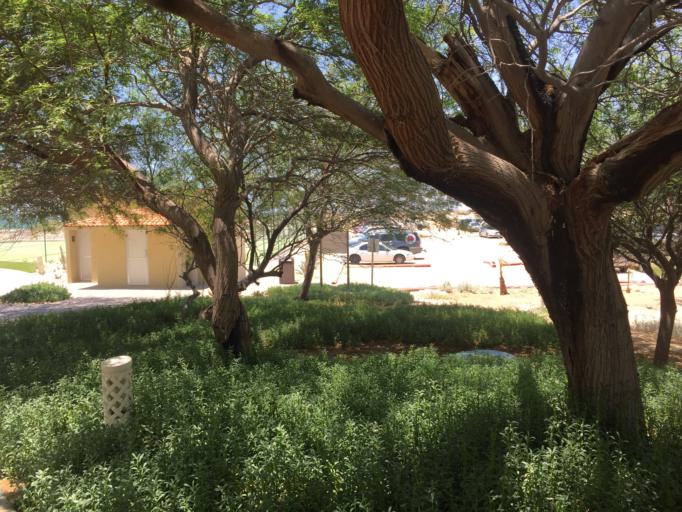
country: MX
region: Sonora
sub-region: Puerto Penasco
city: Puerto Penasco
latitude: 31.2453
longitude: -113.2646
